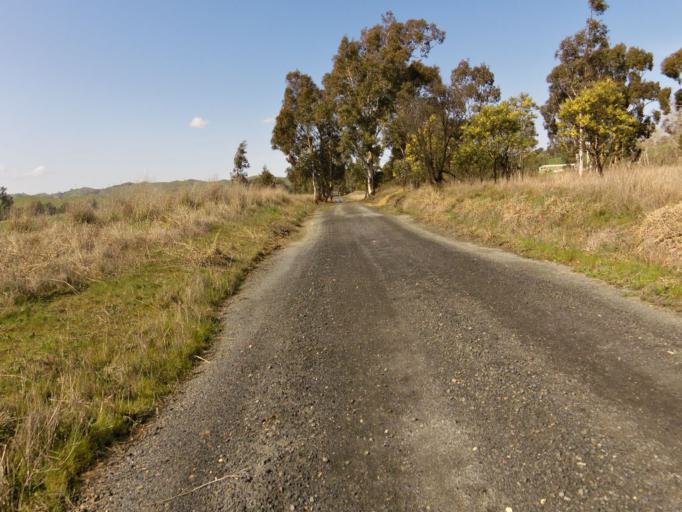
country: AU
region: Victoria
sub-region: Murrindindi
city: Alexandra
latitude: -37.0134
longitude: 145.7671
